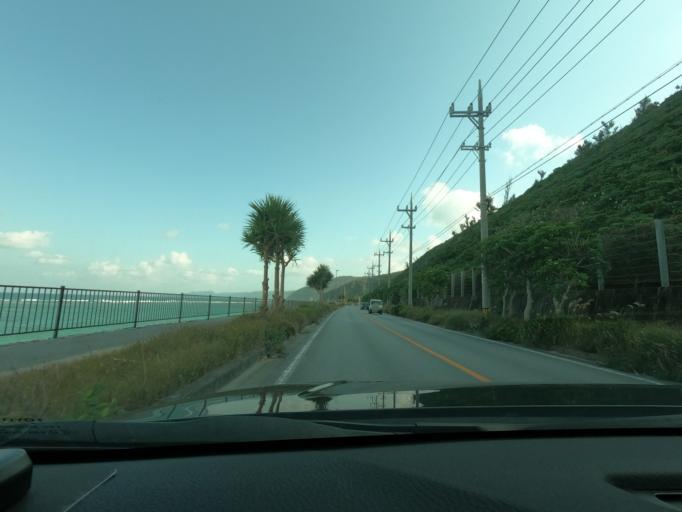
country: JP
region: Okinawa
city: Nago
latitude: 26.7626
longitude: 128.1921
